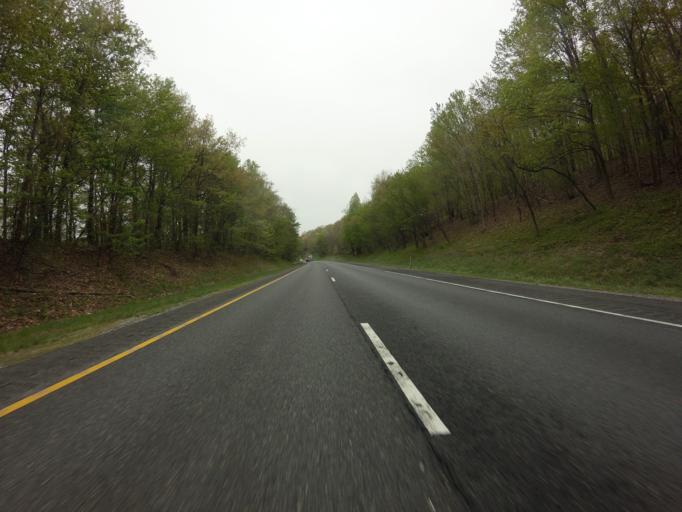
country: US
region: Maryland
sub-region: Frederick County
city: Myersville
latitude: 39.5496
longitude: -77.6087
